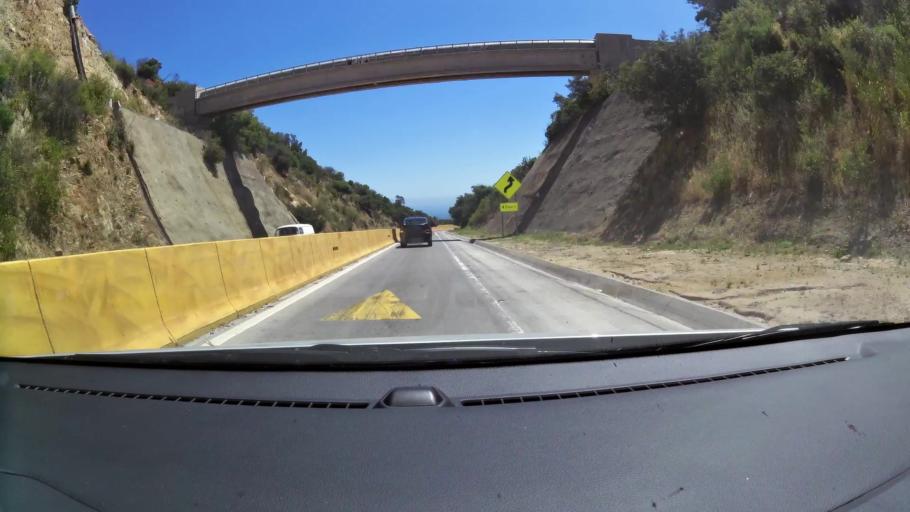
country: CL
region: Valparaiso
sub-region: Provincia de Valparaiso
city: Valparaiso
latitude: -33.0591
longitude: -71.6519
